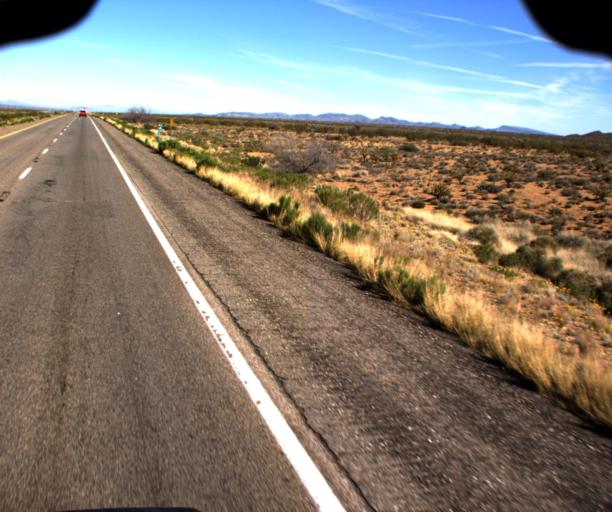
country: US
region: Arizona
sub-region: Mohave County
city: Dolan Springs
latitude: 35.4686
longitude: -114.3100
